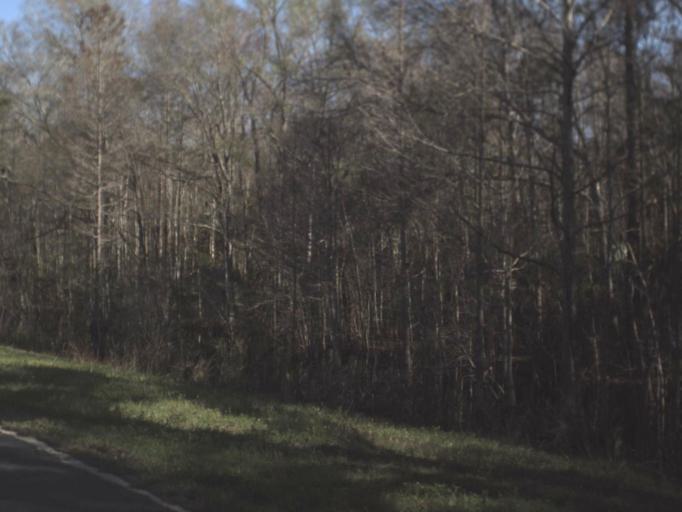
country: US
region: Florida
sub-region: Leon County
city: Woodville
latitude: 30.1785
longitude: -84.0109
